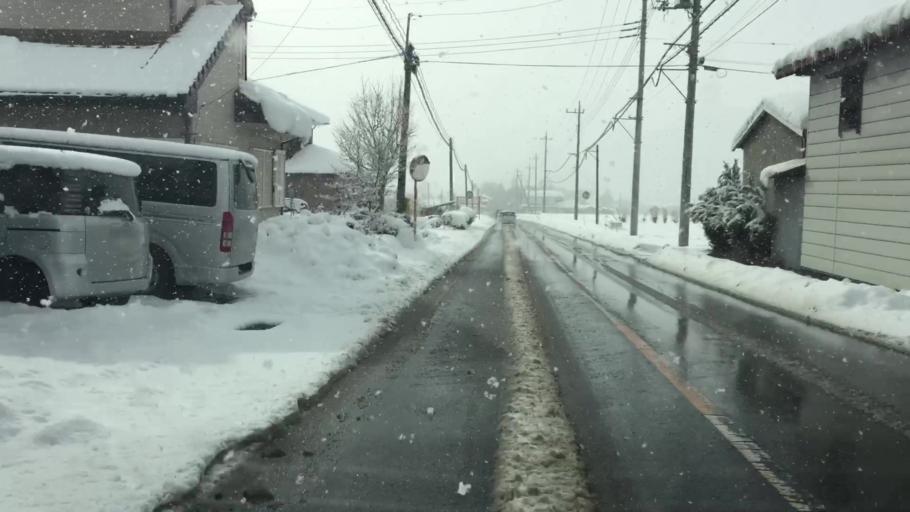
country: JP
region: Gunma
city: Numata
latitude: 36.7038
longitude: 139.0657
